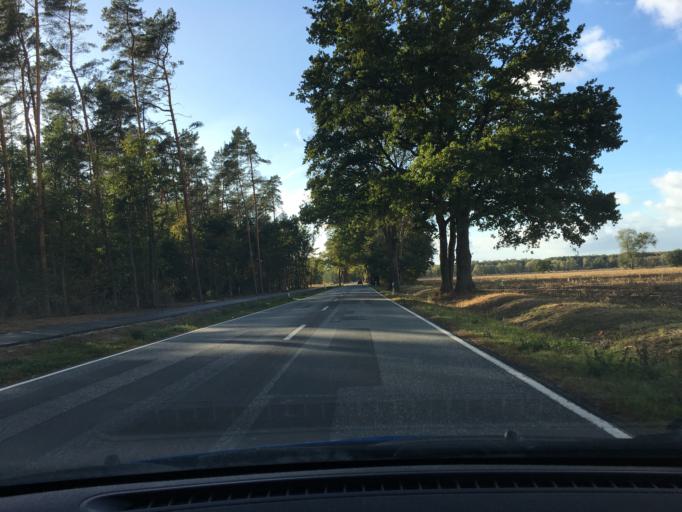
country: DE
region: Mecklenburg-Vorpommern
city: Boizenburg
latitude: 53.3856
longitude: 10.8480
